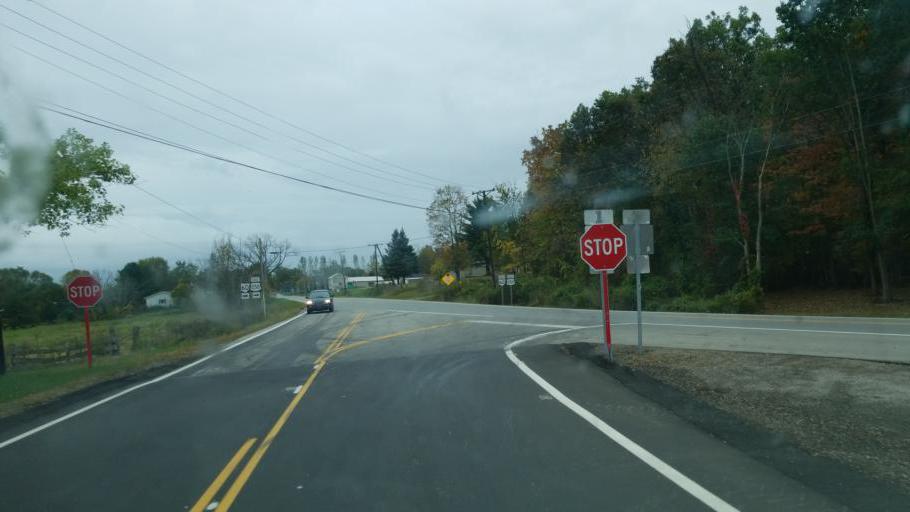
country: US
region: Ohio
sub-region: Huron County
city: New London
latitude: 40.9748
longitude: -82.3670
